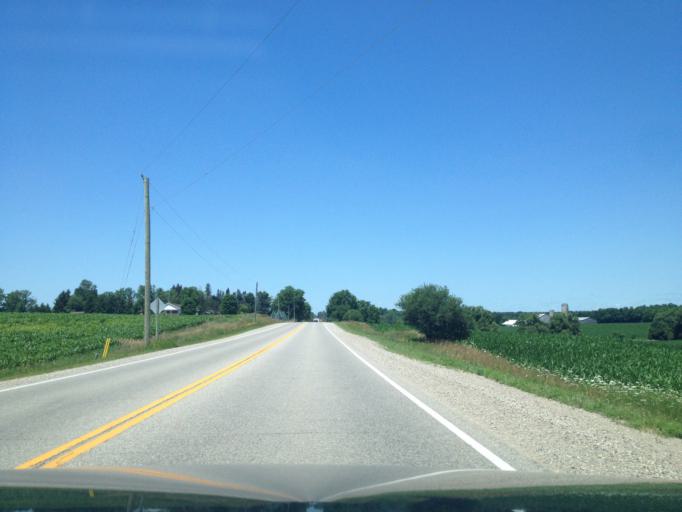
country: CA
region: Ontario
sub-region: Wellington County
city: Guelph
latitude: 43.6226
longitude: -80.2239
